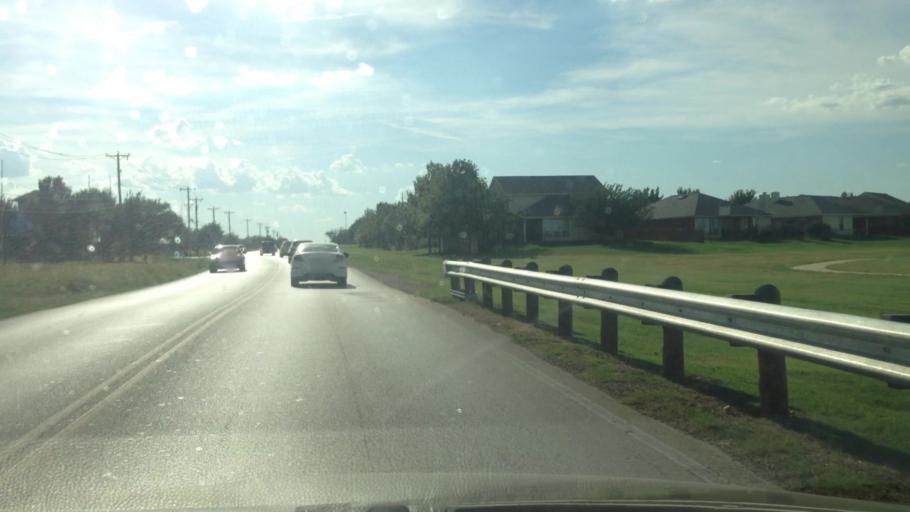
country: US
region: Texas
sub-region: Tarrant County
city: Haslet
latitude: 32.9244
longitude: -97.3643
